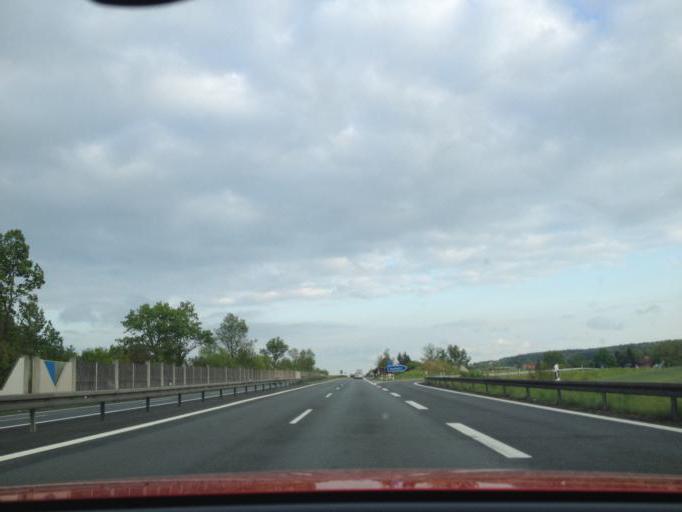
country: DE
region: Bavaria
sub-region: Upper Palatinate
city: Weiden
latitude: 49.6755
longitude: 12.1297
